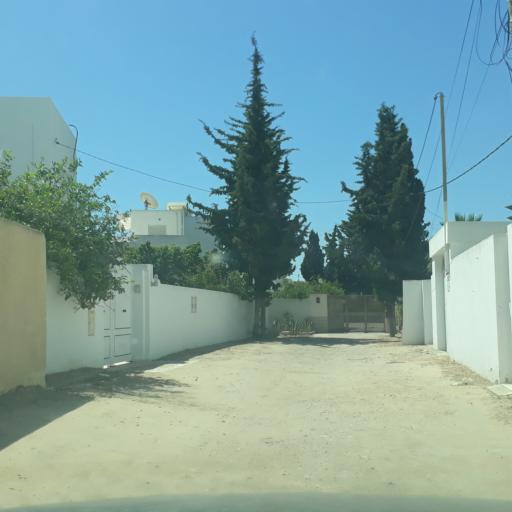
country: TN
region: Safaqis
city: Al Qarmadah
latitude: 34.7994
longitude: 10.7590
